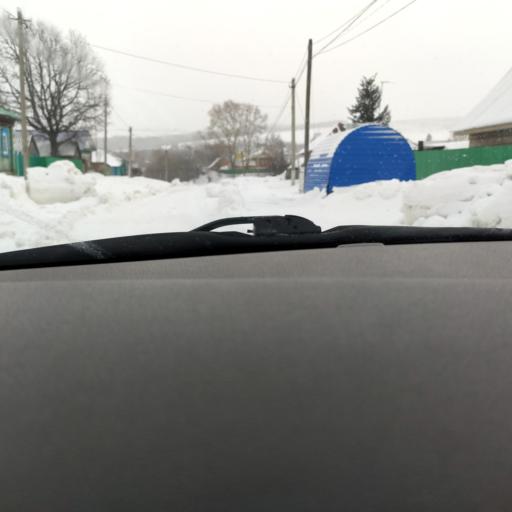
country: RU
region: Bashkortostan
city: Blagoveshchensk
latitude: 55.1725
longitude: 55.8360
